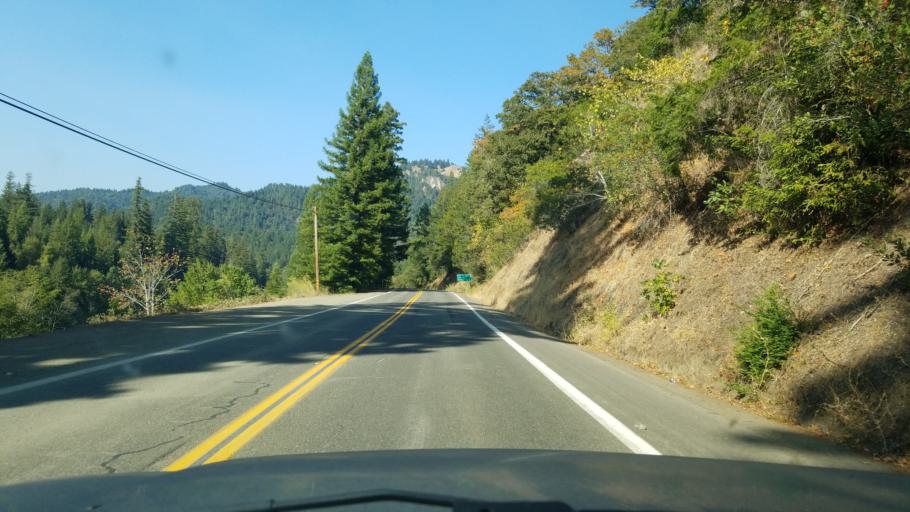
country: US
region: California
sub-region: Humboldt County
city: Redway
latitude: 40.1835
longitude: -123.7731
